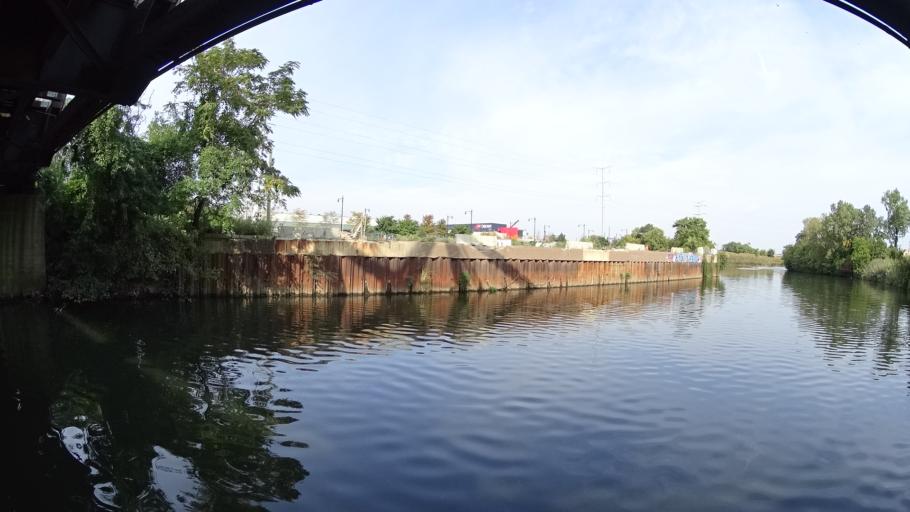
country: US
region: Illinois
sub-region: Cook County
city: Chicago
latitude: 41.8397
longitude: -87.6648
